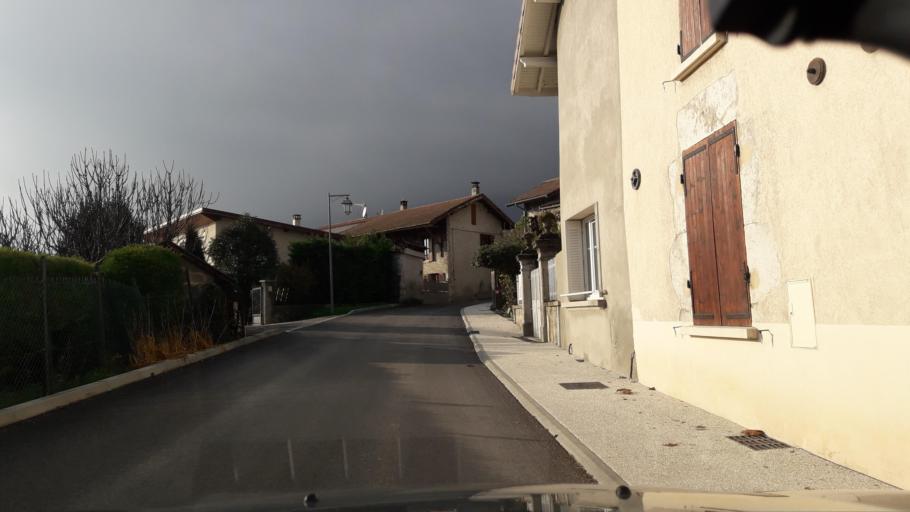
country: FR
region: Rhone-Alpes
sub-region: Departement de l'Isere
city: Saint-Ismier
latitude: 45.2457
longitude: 5.8395
